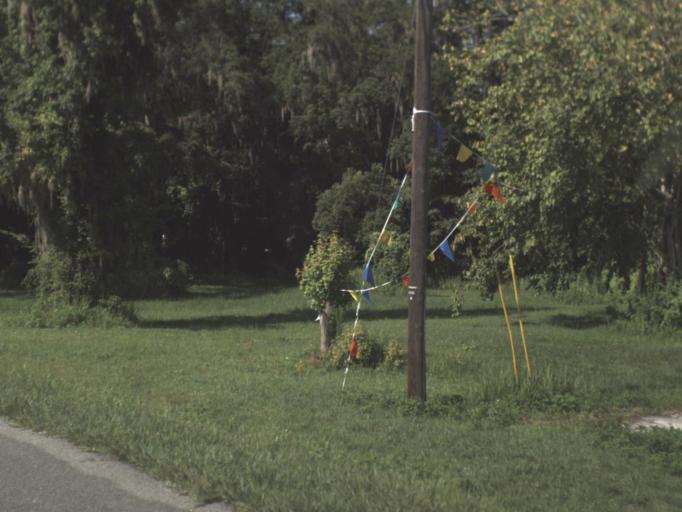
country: US
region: Florida
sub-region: Hernando County
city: Brooksville
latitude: 28.5587
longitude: -82.3977
